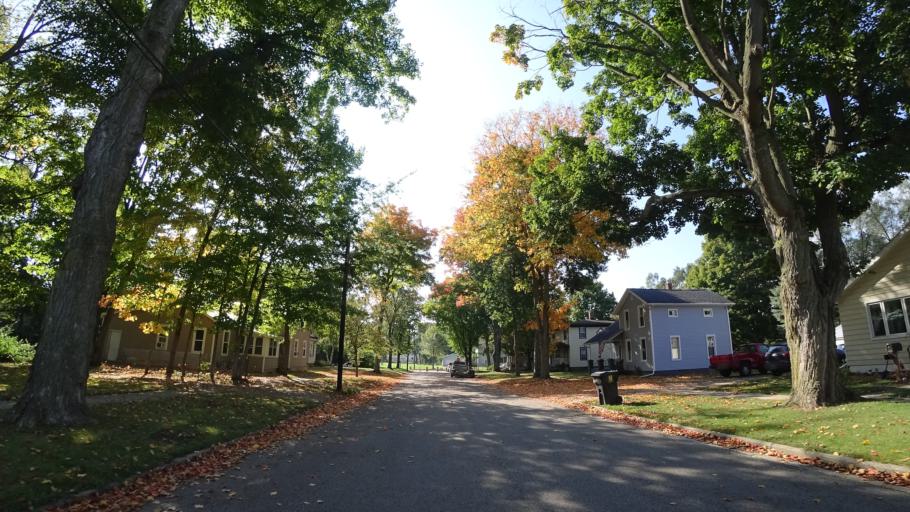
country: US
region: Michigan
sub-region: Saint Joseph County
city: Three Rivers
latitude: 41.9409
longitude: -85.6382
